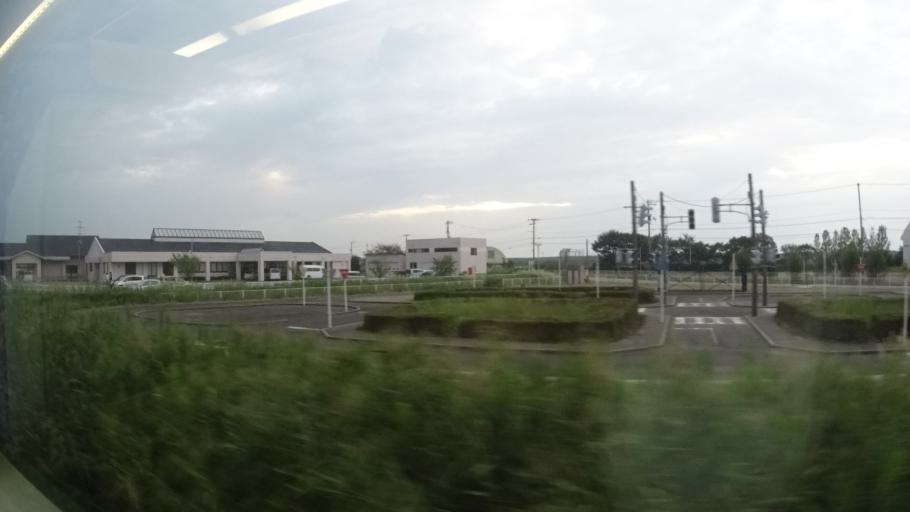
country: JP
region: Niigata
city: Murakami
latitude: 38.1776
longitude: 139.4595
